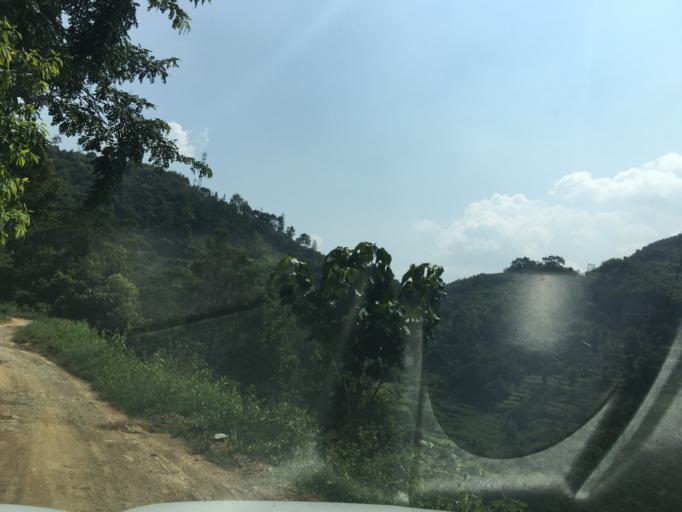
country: CN
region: Guangxi Zhuangzu Zizhiqu
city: Xinzhou
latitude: 24.9902
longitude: 105.7384
